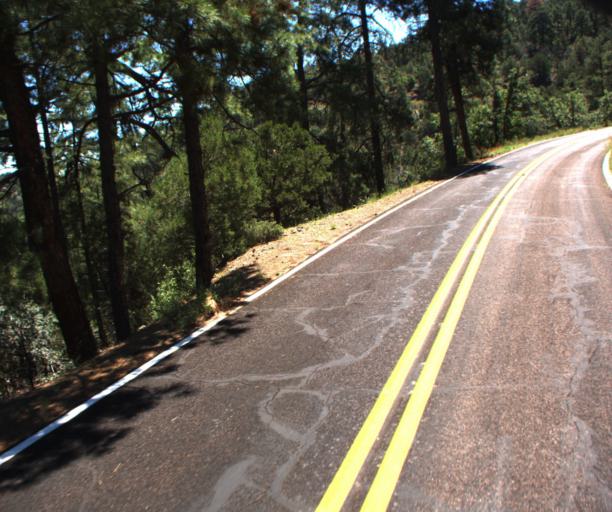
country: US
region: Arizona
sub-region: Greenlee County
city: Morenci
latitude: 33.4109
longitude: -109.3568
